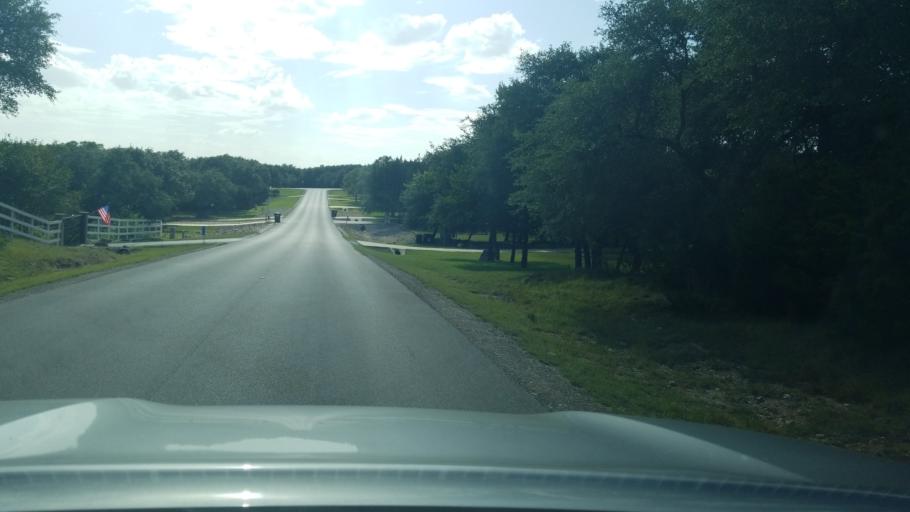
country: US
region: Texas
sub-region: Comal County
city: Bulverde
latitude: 29.8053
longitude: -98.4069
